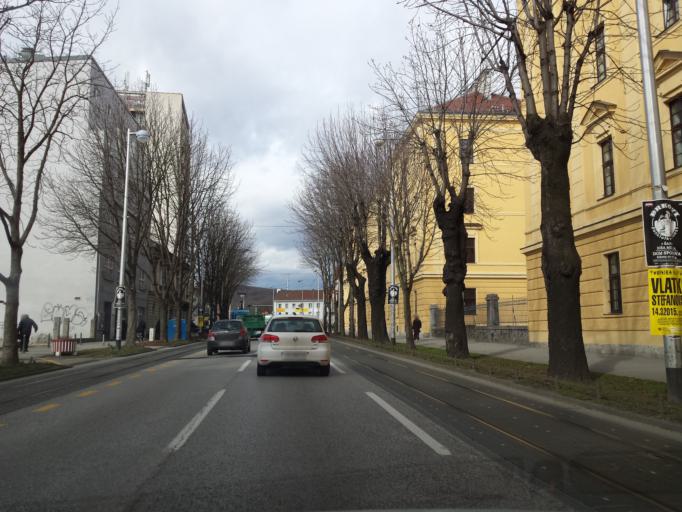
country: HR
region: Grad Zagreb
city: Zagreb - Centar
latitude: 45.8145
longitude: 15.9377
